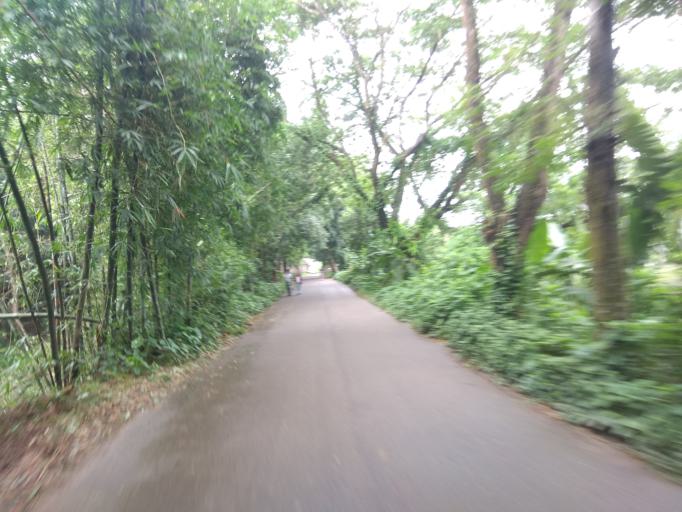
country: BD
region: Dhaka
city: Dohar
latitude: 23.4260
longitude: 90.0648
